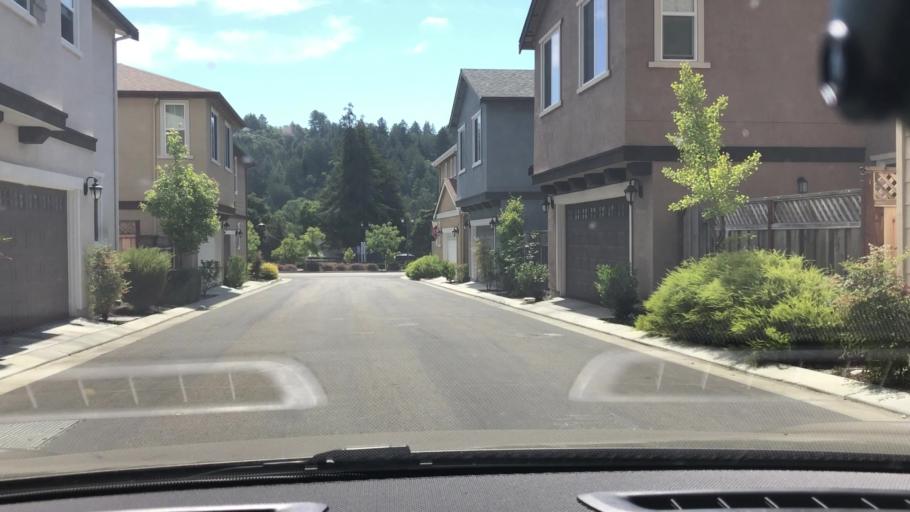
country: US
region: California
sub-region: Santa Cruz County
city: Scotts Valley
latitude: 37.0542
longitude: -122.0141
